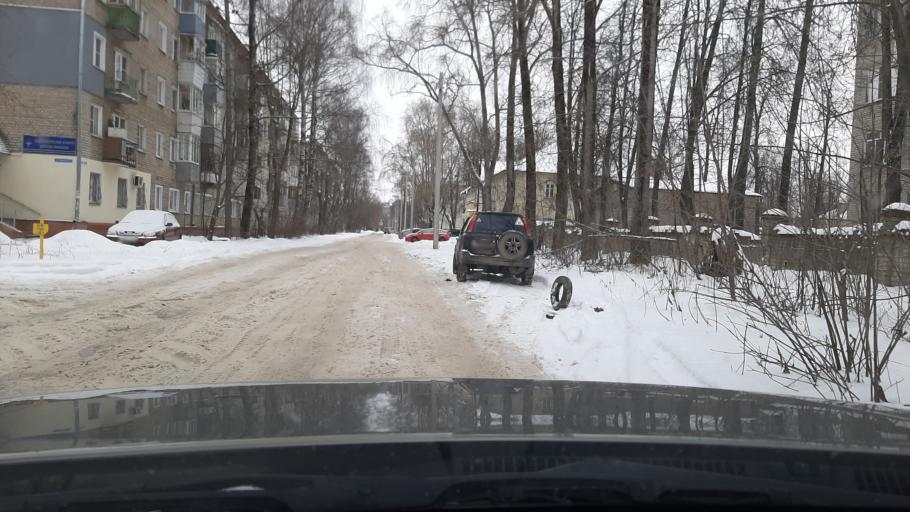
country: RU
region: Ivanovo
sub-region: Gorod Ivanovo
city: Ivanovo
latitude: 56.9714
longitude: 40.9681
